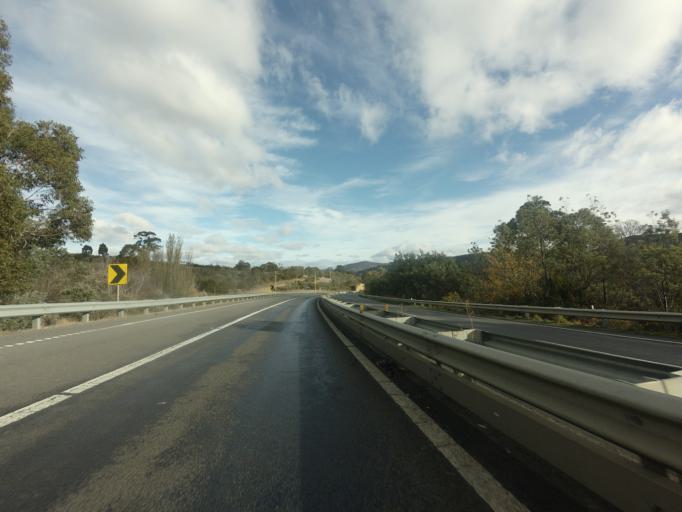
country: AU
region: Tasmania
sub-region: Brighton
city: Bridgewater
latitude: -42.5819
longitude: 147.2289
